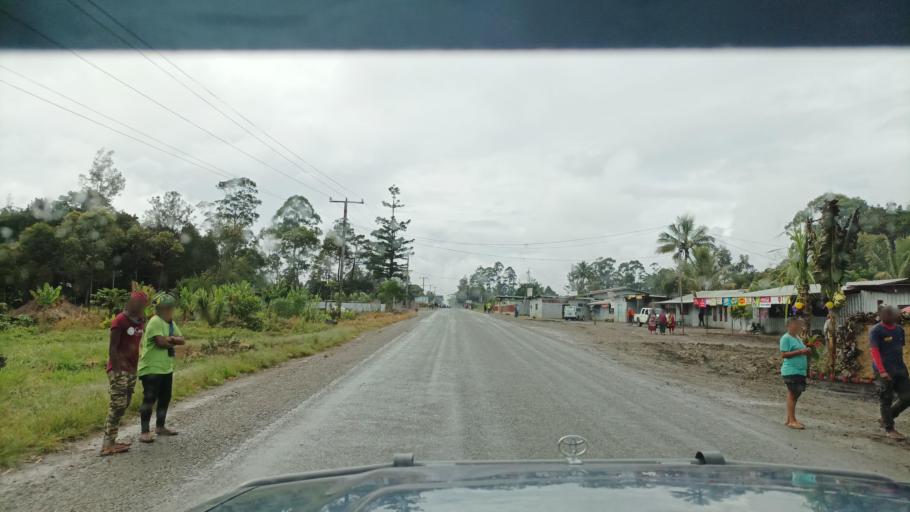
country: PG
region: Jiwaka
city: Minj
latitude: -5.8786
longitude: 144.6743
